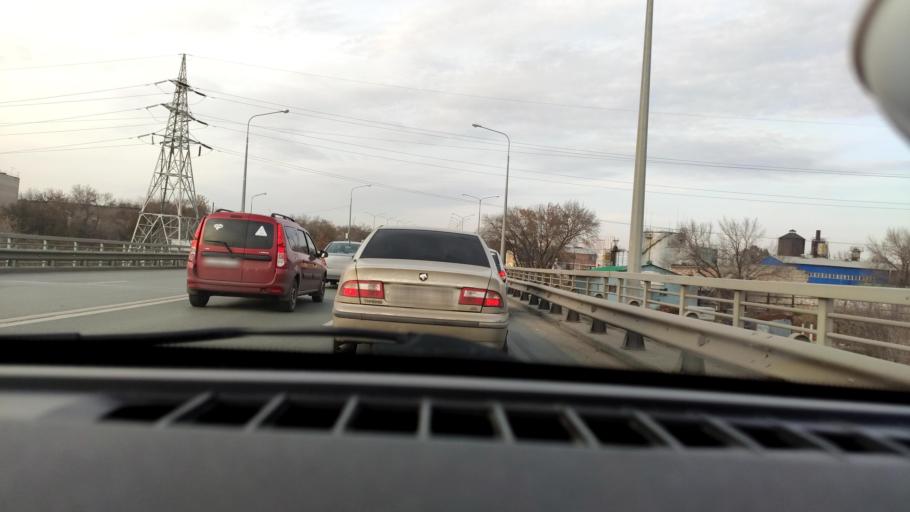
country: RU
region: Samara
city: Samara
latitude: 53.1672
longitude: 50.1911
